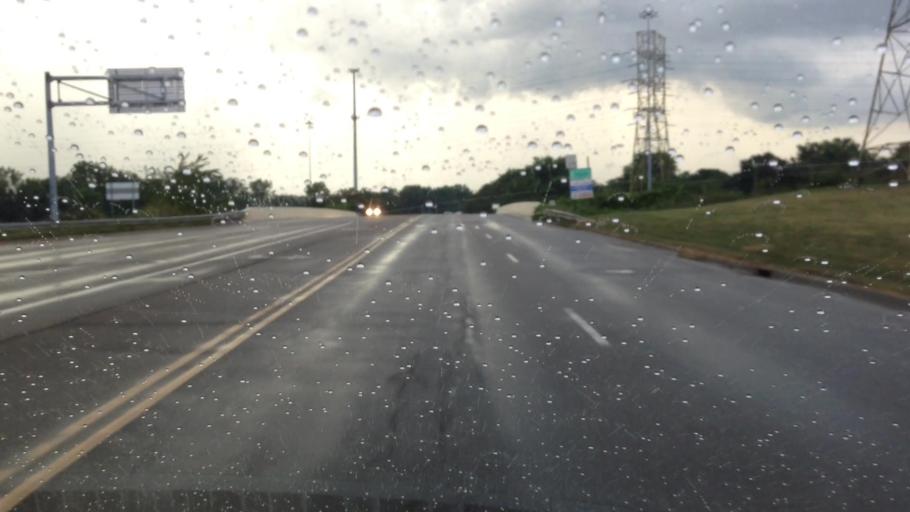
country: US
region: Ohio
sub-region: Summit County
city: Portage Lakes
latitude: 41.0241
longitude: -81.5263
